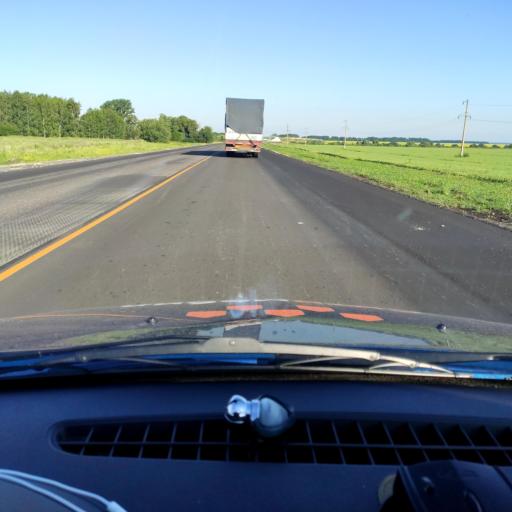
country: RU
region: Orjol
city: Zmiyevka
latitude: 52.6959
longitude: 36.3874
